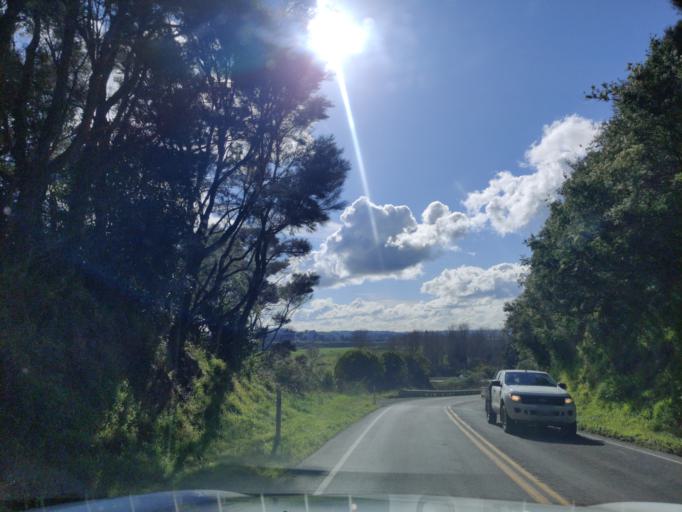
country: NZ
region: Manawatu-Wanganui
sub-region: Palmerston North City
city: Palmerston North
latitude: -40.2834
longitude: 175.7717
